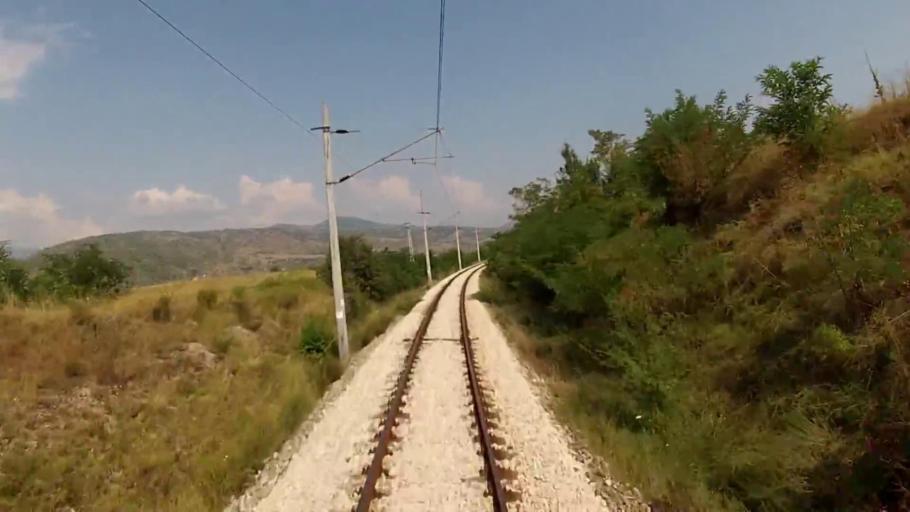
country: BG
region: Blagoevgrad
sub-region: Obshtina Sandanski
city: Sandanski
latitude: 41.5300
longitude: 23.2593
